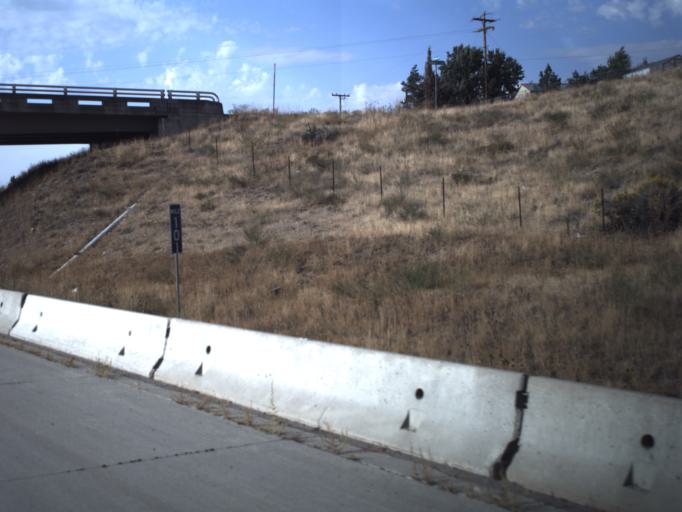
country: US
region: Utah
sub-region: Morgan County
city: Morgan
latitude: 41.0662
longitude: -111.7109
